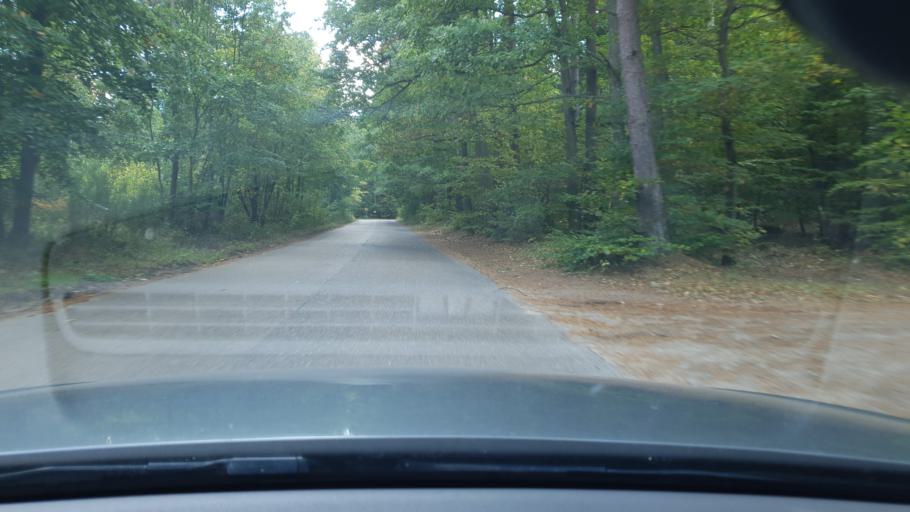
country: PL
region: Pomeranian Voivodeship
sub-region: Powiat wejherowski
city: Reda
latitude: 54.5907
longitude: 18.3353
